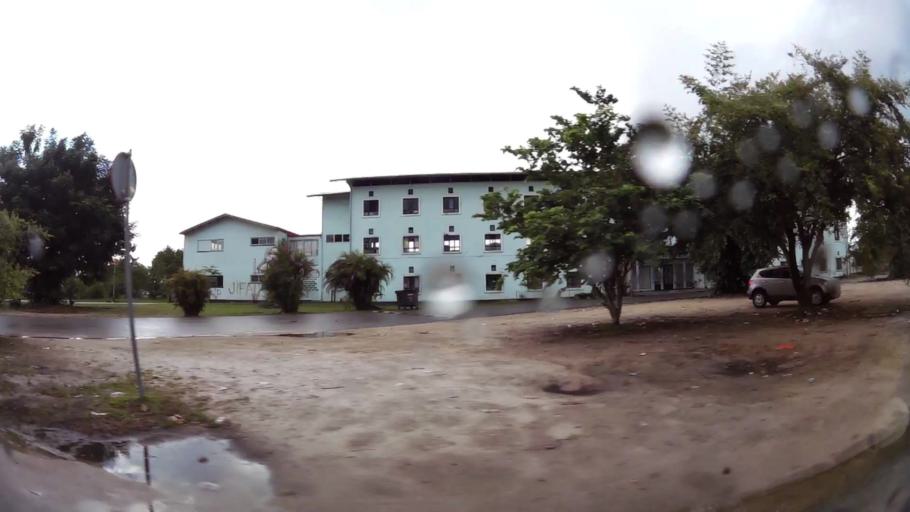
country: SR
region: Paramaribo
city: Paramaribo
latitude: 5.8151
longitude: -55.1807
